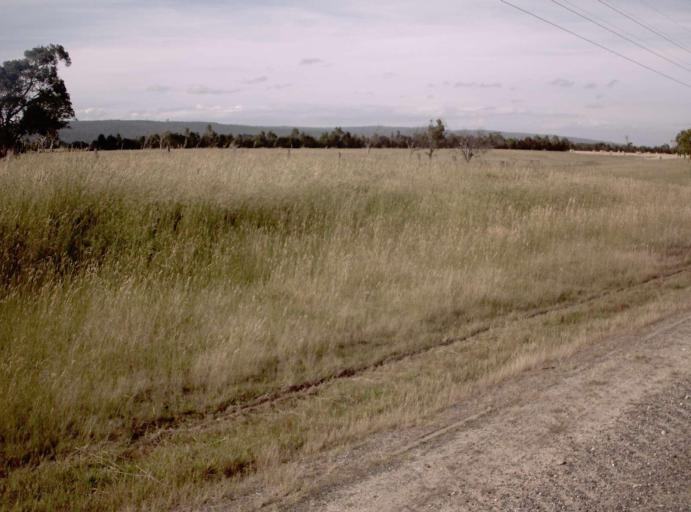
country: AU
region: Victoria
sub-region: Latrobe
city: Traralgon
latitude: -38.1138
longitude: 146.5821
